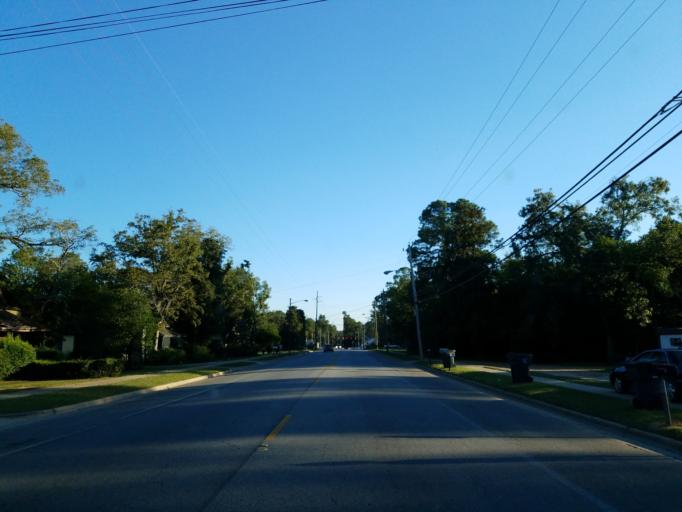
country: US
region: Georgia
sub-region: Worth County
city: Sylvester
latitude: 31.5336
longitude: -83.8441
